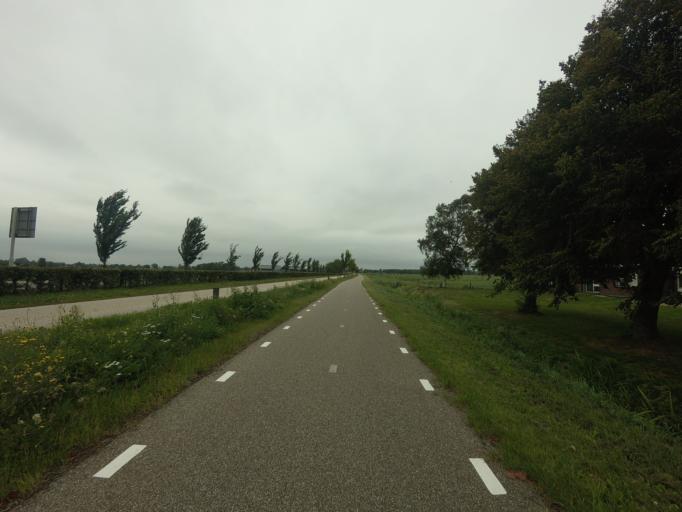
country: NL
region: Friesland
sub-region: Gemeente Opsterland
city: Gorredijk
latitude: 53.0081
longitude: 6.0390
